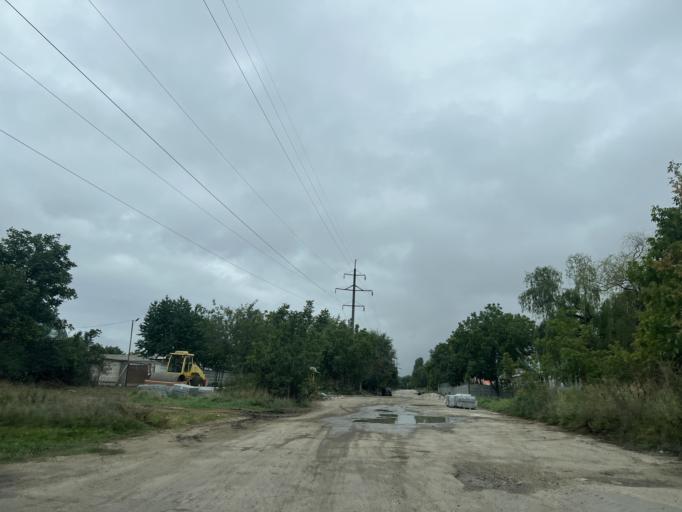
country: MD
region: Ungheni
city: Ungheni
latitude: 47.2256
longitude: 27.8053
